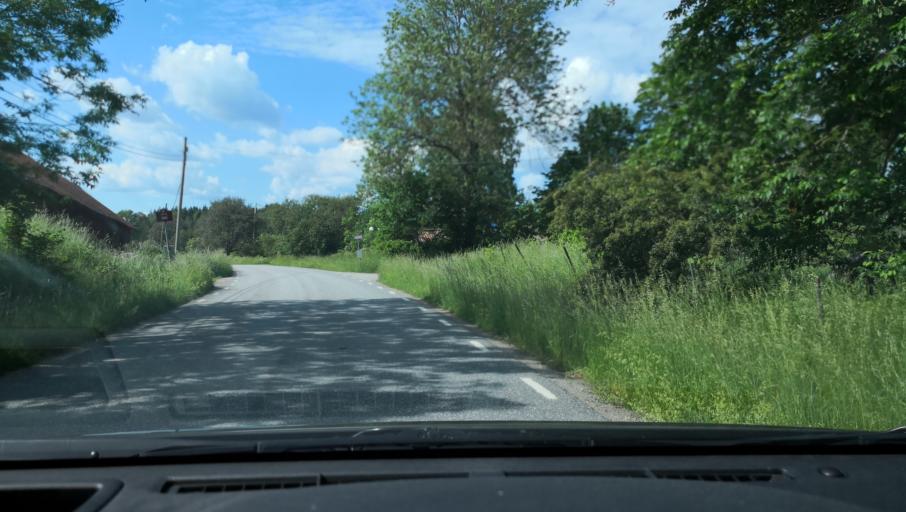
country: SE
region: Uppsala
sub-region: Enkopings Kommun
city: Orsundsbro
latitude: 59.8312
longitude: 17.3188
